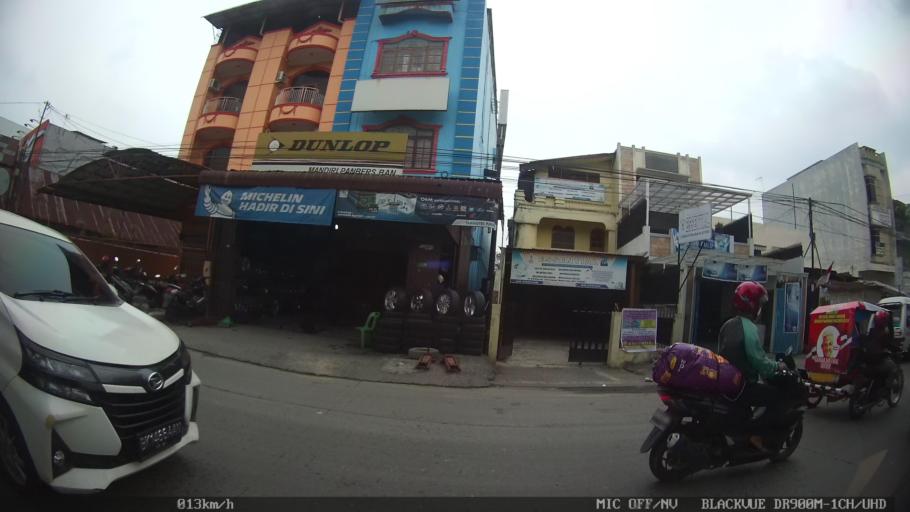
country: ID
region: North Sumatra
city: Medan
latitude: 3.5636
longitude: 98.6926
